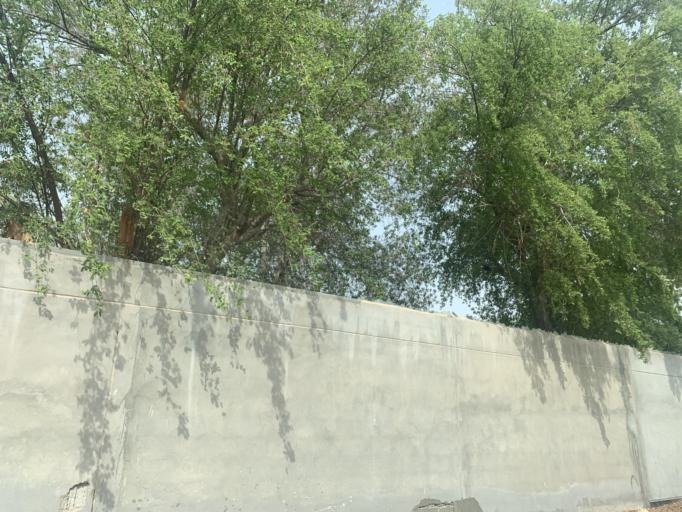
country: BH
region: Manama
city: Jidd Hafs
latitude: 26.2002
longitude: 50.4786
